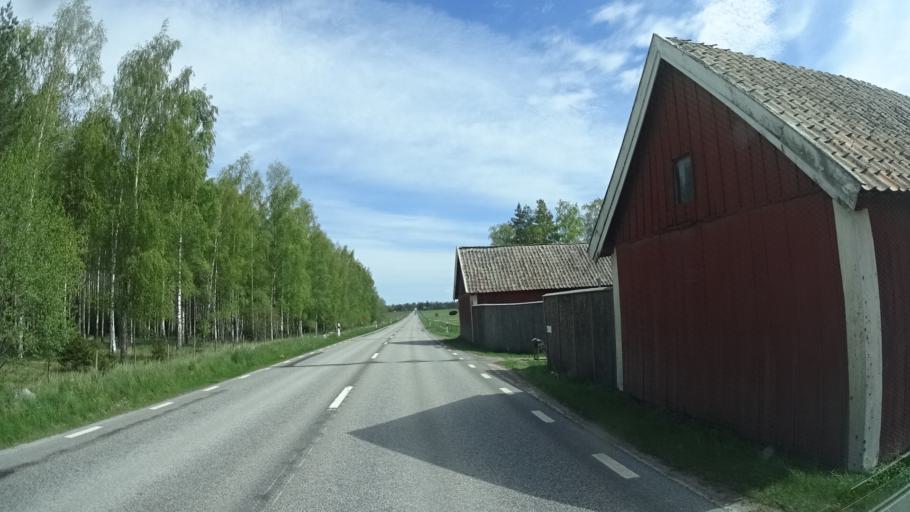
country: SE
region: OEstergoetland
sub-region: Mjolby Kommun
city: Mantorp
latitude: 58.3697
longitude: 15.3492
